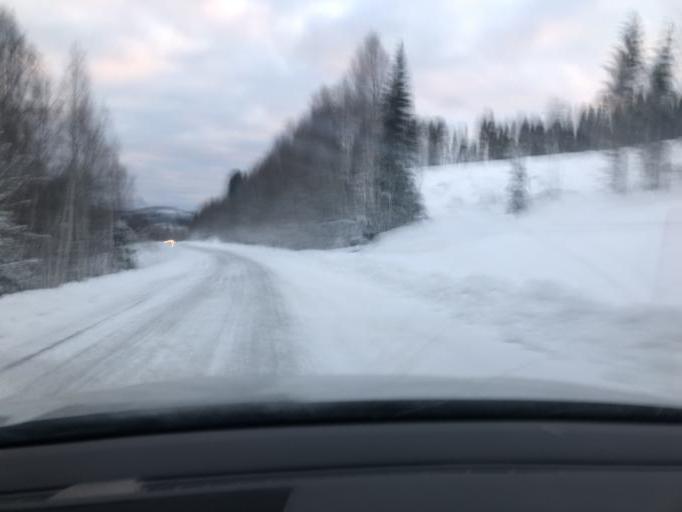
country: SE
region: Vaesternorrland
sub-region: Kramfors Kommun
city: Nordingra
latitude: 62.9721
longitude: 18.2546
